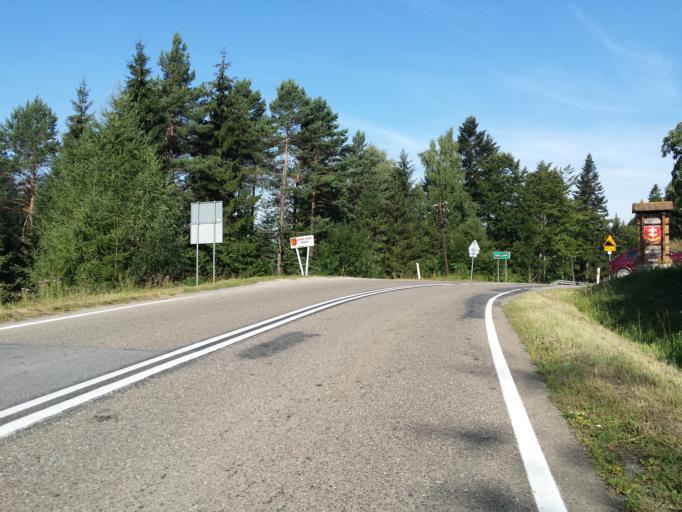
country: PL
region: Subcarpathian Voivodeship
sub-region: Powiat leski
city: Cisna
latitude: 49.2414
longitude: 22.2975
